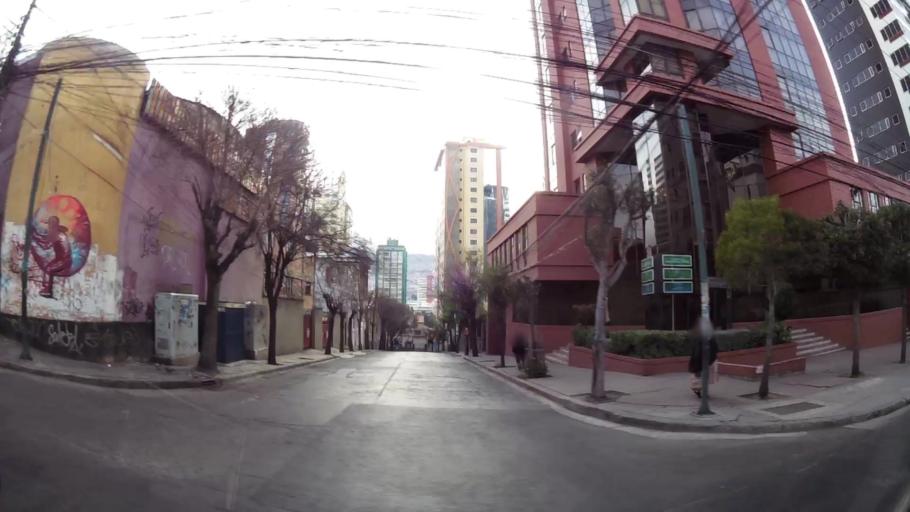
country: BO
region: La Paz
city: La Paz
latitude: -16.5120
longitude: -68.1246
